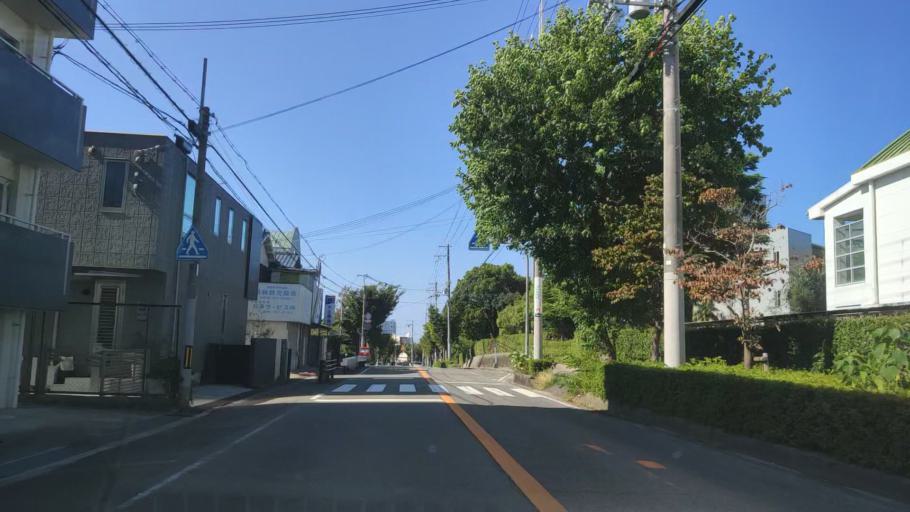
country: JP
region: Hyogo
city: Akashi
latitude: 34.6577
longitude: 135.0095
